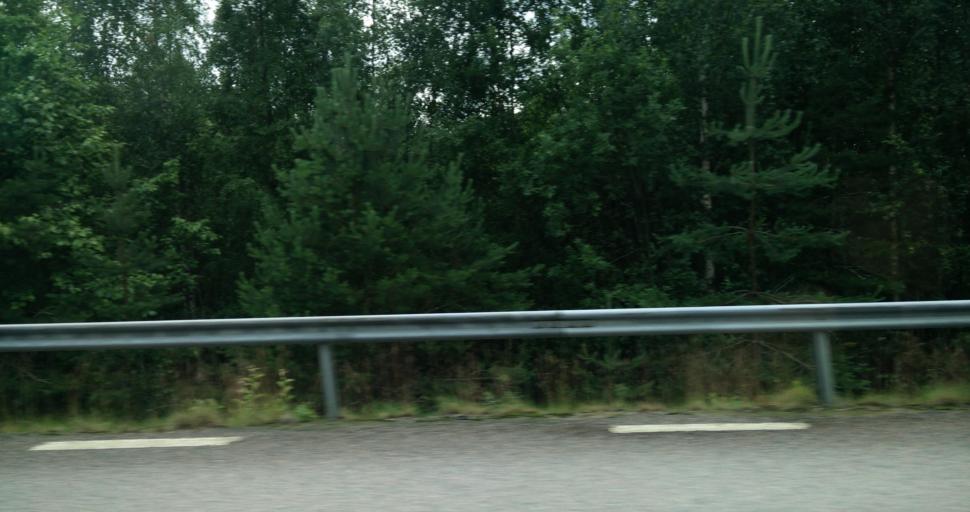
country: SE
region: Vaermland
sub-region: Munkfors Kommun
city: Munkfors
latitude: 59.9707
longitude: 13.5399
